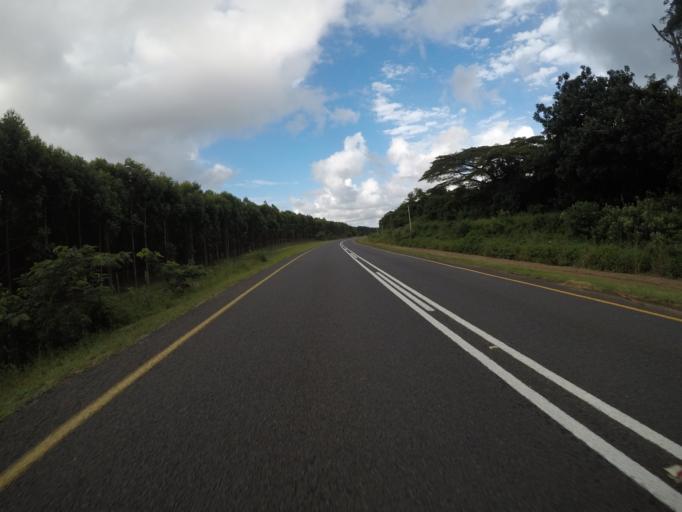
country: ZA
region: KwaZulu-Natal
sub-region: uMkhanyakude District Municipality
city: Mtubatuba
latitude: -28.3709
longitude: 32.2555
